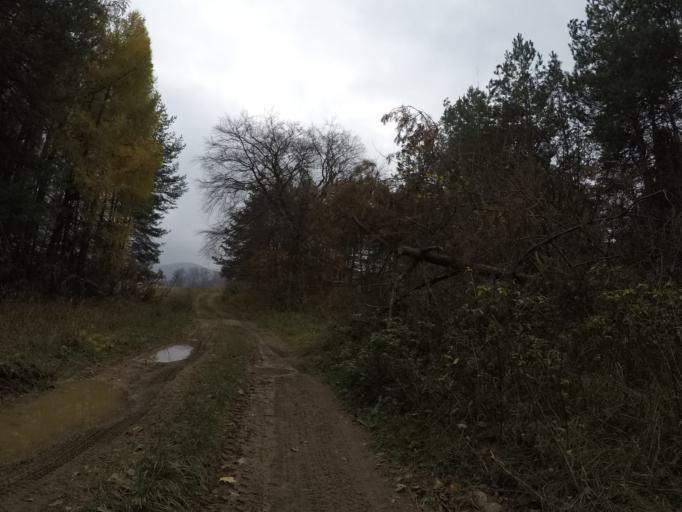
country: SK
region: Presovsky
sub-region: Okres Presov
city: Presov
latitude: 48.8952
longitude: 21.1721
